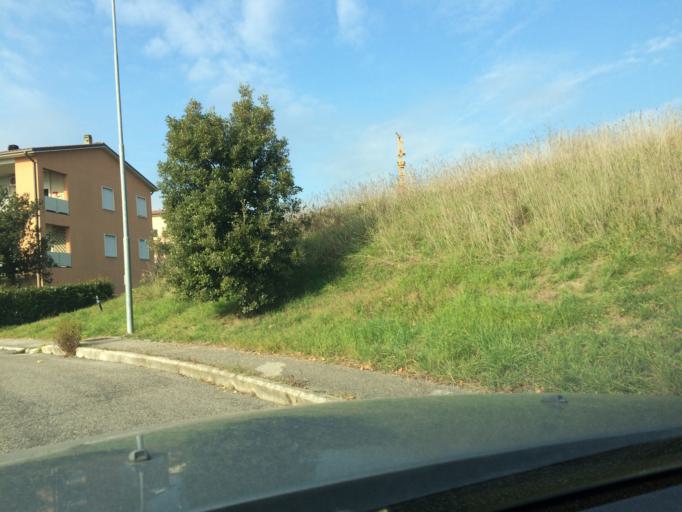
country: IT
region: Umbria
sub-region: Provincia di Perugia
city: Via Lippia
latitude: 43.1008
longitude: 12.4927
